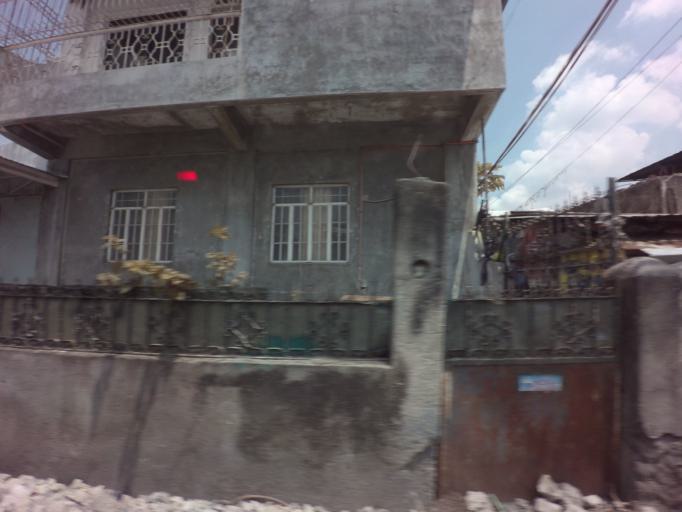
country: PH
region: Calabarzon
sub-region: Province of Laguna
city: San Pedro
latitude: 14.4036
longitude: 121.0502
